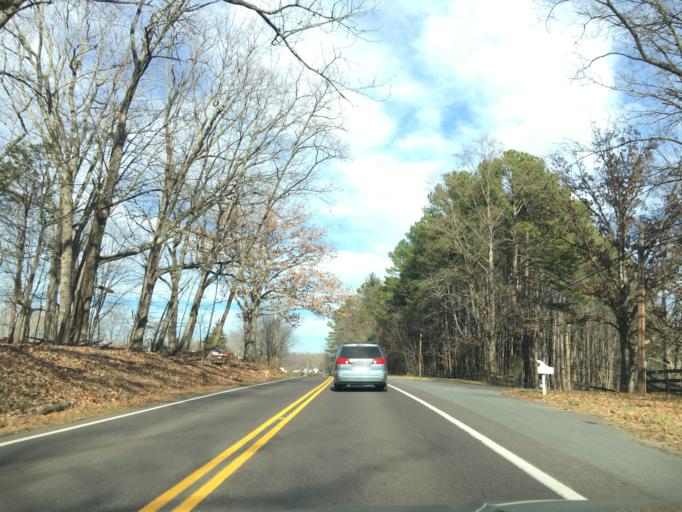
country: US
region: Virginia
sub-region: Culpeper County
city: Culpeper
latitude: 38.5191
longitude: -77.9847
